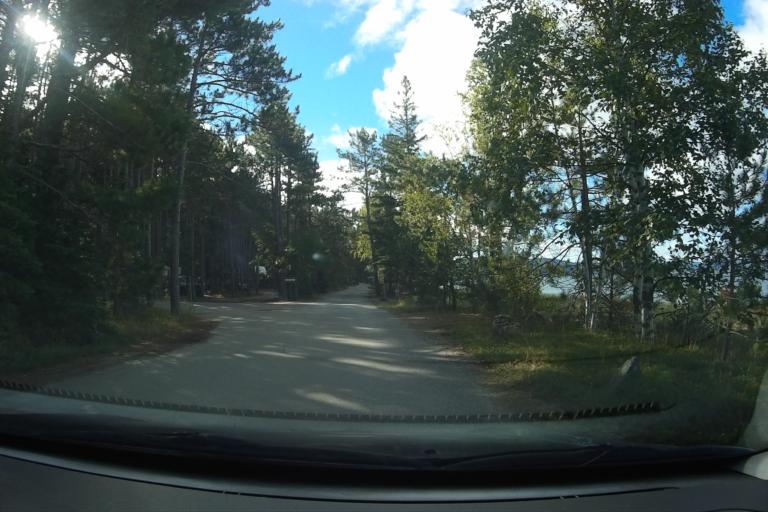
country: CA
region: Ontario
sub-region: Algoma
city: Sault Ste. Marie
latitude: 47.3307
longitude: -84.6142
